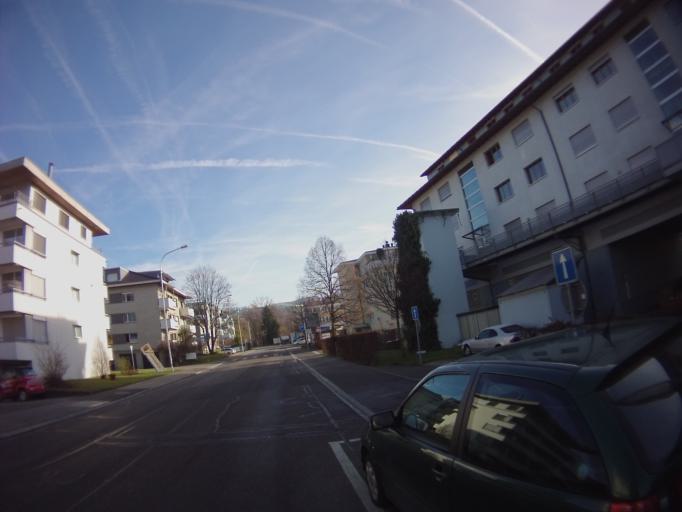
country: CH
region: Zug
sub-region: Zug
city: Zug
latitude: 47.1827
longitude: 8.5248
